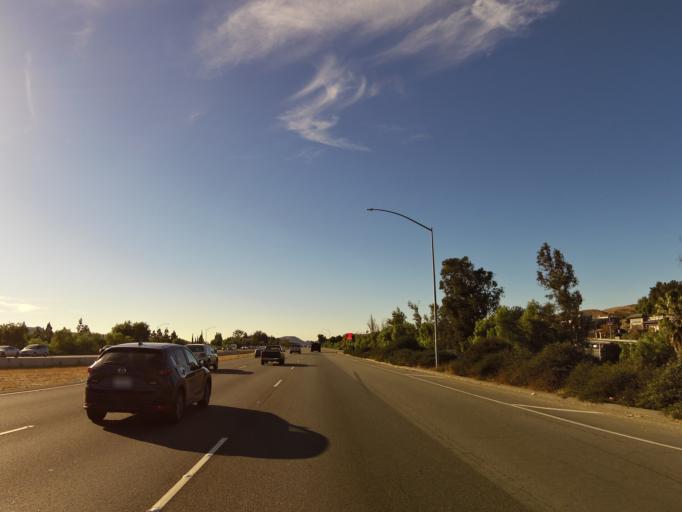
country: US
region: California
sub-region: Ventura County
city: Simi Valley
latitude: 34.2824
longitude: -118.7622
